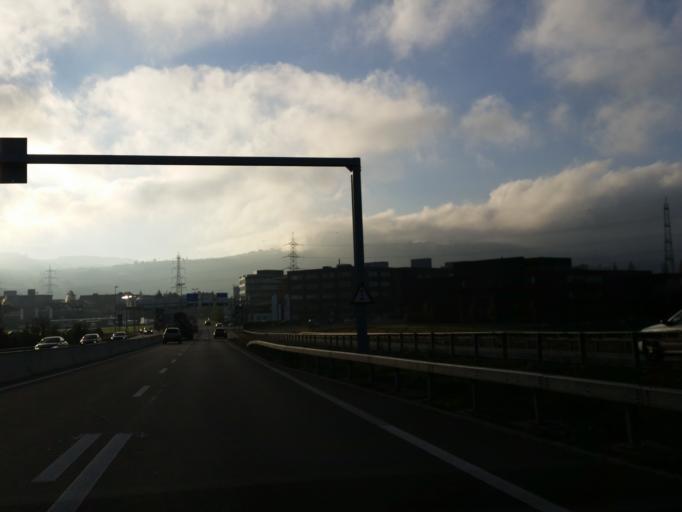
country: CH
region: Zug
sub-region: Zug
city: Baar
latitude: 47.1939
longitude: 8.5119
